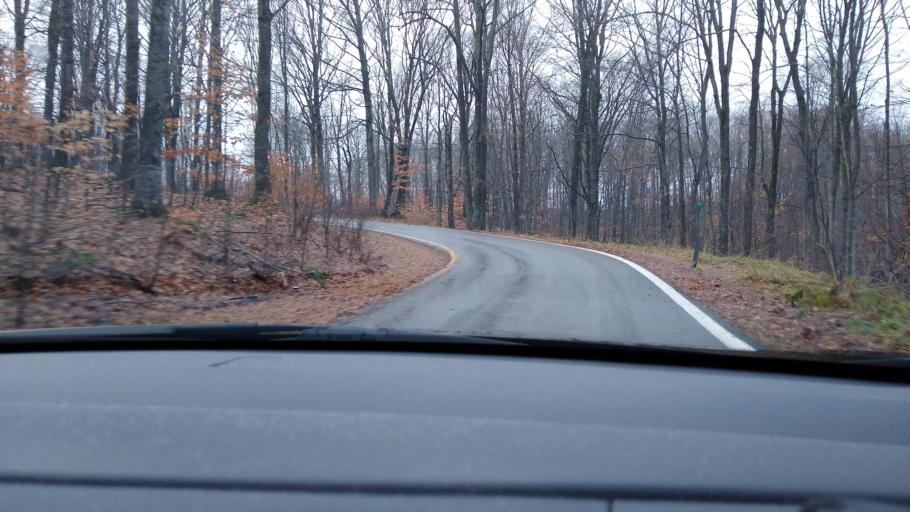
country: US
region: Michigan
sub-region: Otsego County
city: Gaylord
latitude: 45.1079
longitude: -84.6896
